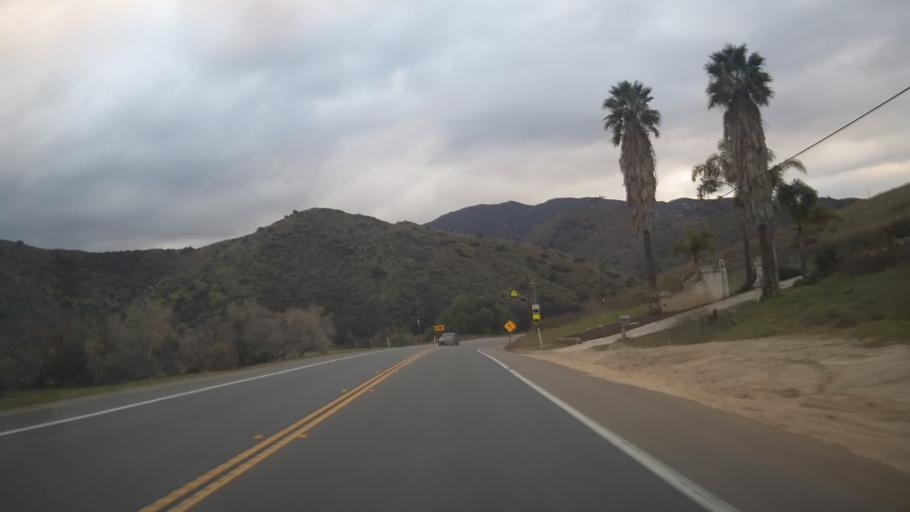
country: US
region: California
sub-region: San Diego County
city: Crest
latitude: 32.7829
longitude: -116.8470
